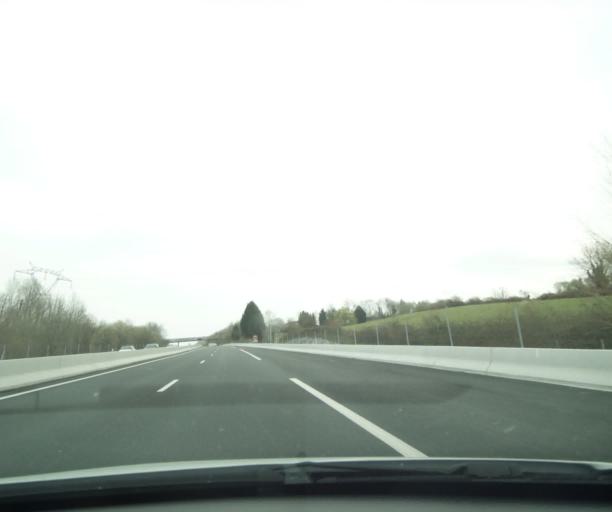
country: FR
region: Aquitaine
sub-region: Departement des Pyrenees-Atlantiques
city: Lahonce
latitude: 43.4476
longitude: -1.3739
